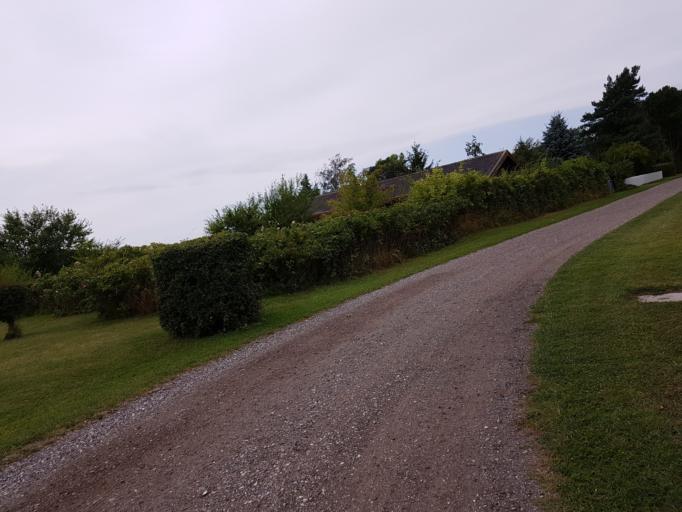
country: DK
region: Zealand
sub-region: Guldborgsund Kommune
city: Nykobing Falster
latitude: 54.5892
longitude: 11.9624
